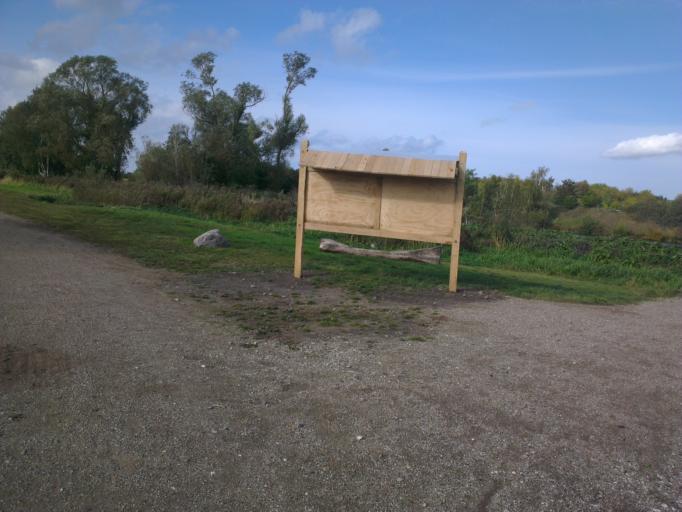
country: DK
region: Capital Region
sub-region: Frederikssund Kommune
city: Frederikssund
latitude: 55.8316
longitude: 12.0898
